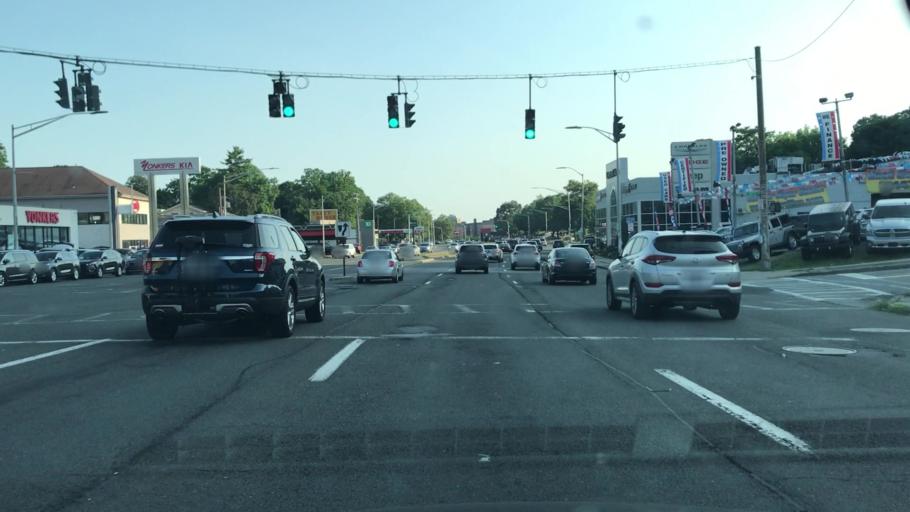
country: US
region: New York
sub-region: Westchester County
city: Tuckahoe
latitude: 40.9625
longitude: -73.8400
